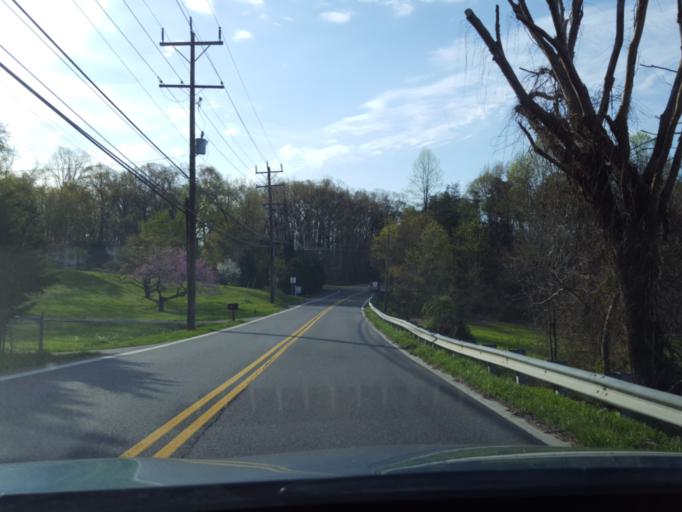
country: US
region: Maryland
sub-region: Prince George's County
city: Croom
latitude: 38.7706
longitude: -76.7592
